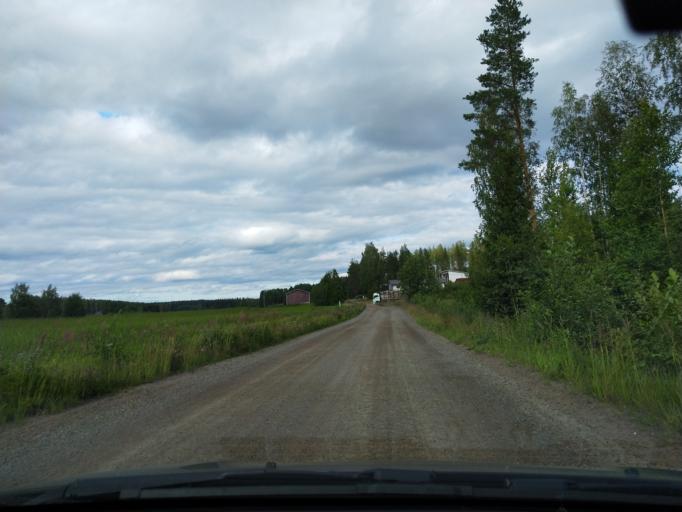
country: FI
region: Kymenlaakso
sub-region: Kouvola
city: Kouvola
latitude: 61.0526
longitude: 26.8665
